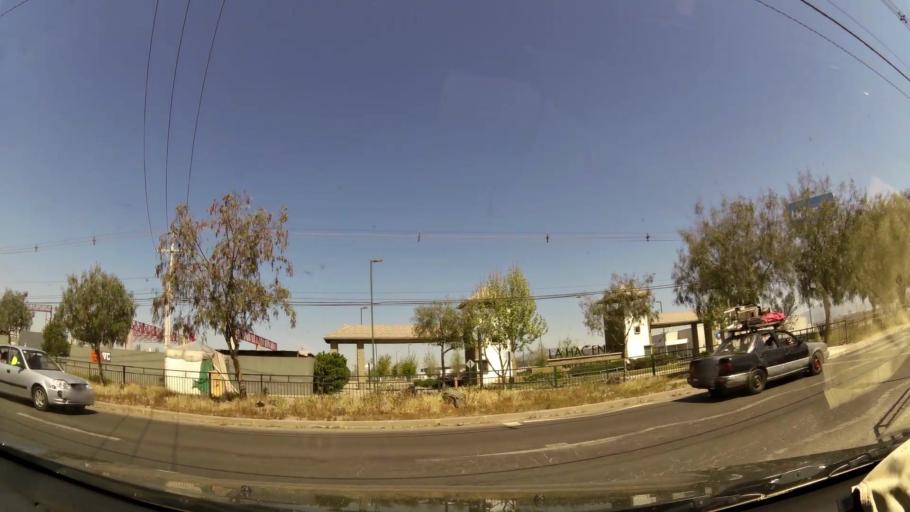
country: CL
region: Santiago Metropolitan
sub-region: Provincia de Santiago
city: Lo Prado
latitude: -33.3990
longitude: -70.7571
